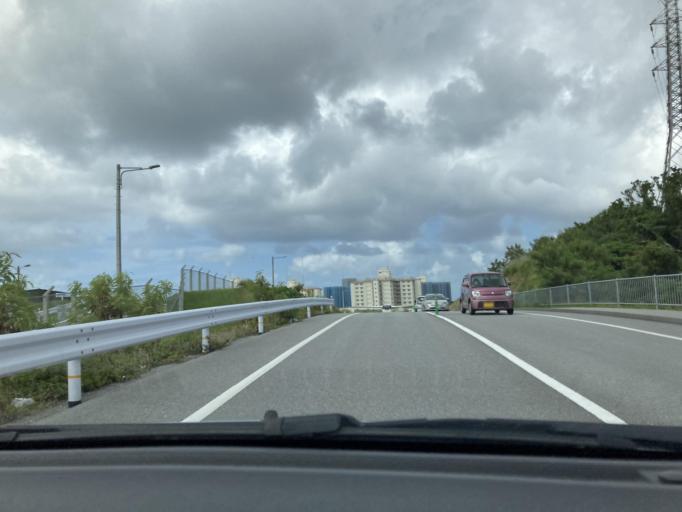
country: JP
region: Okinawa
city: Ginowan
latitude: 26.2628
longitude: 127.7086
